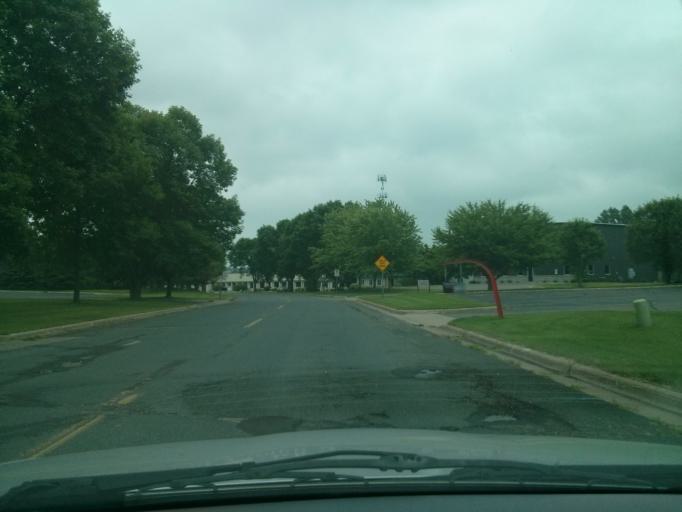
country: US
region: Minnesota
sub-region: Washington County
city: Lakeland
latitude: 44.9542
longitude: -92.7387
